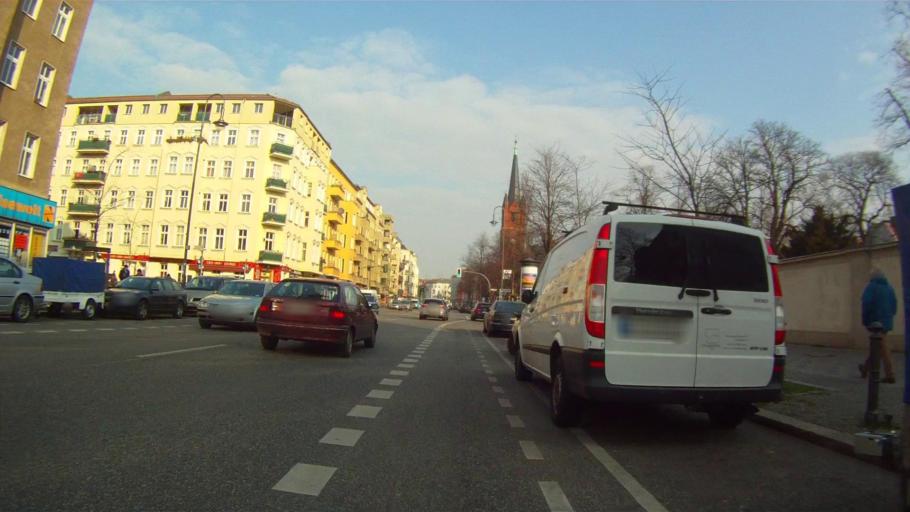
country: DE
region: Berlin
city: Berlin Treptow
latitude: 52.4708
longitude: 13.4415
